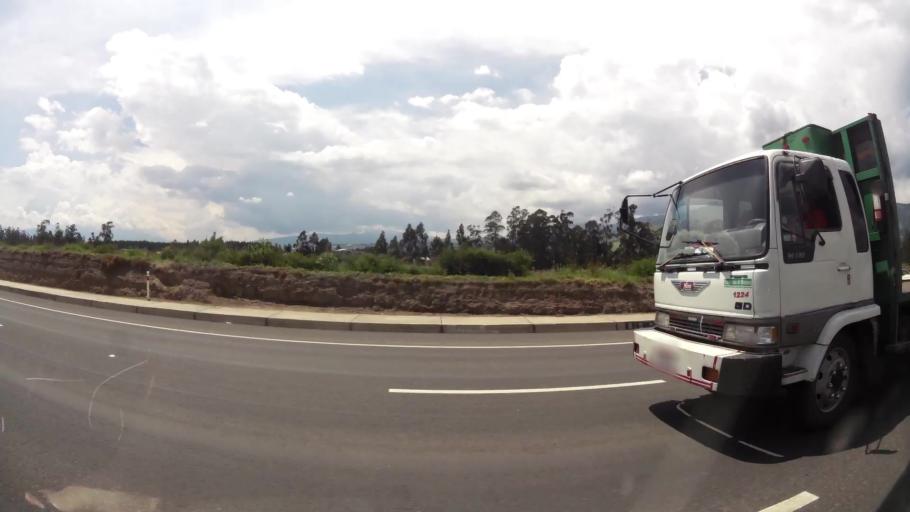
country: EC
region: Pichincha
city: Sangolqui
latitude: -0.1978
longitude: -78.3380
